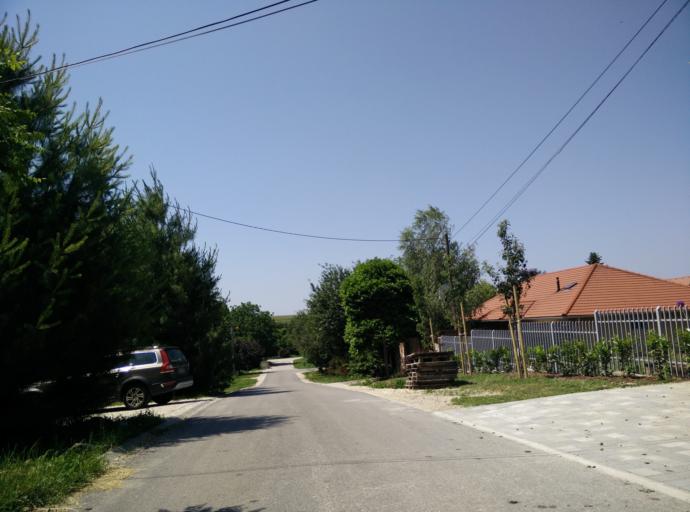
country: HU
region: Pest
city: Biatorbagy
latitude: 47.4609
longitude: 18.8211
